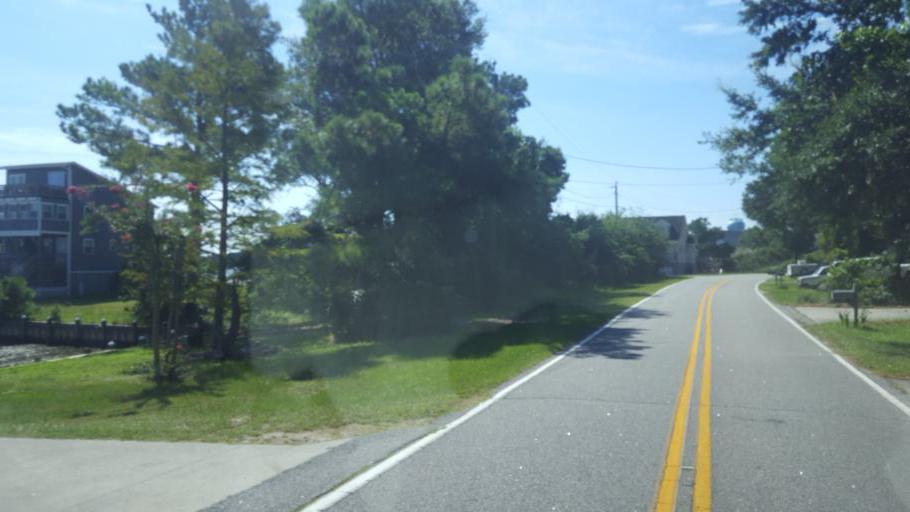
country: US
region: North Carolina
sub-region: Dare County
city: Kill Devil Hills
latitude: 36.0159
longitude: -75.7109
